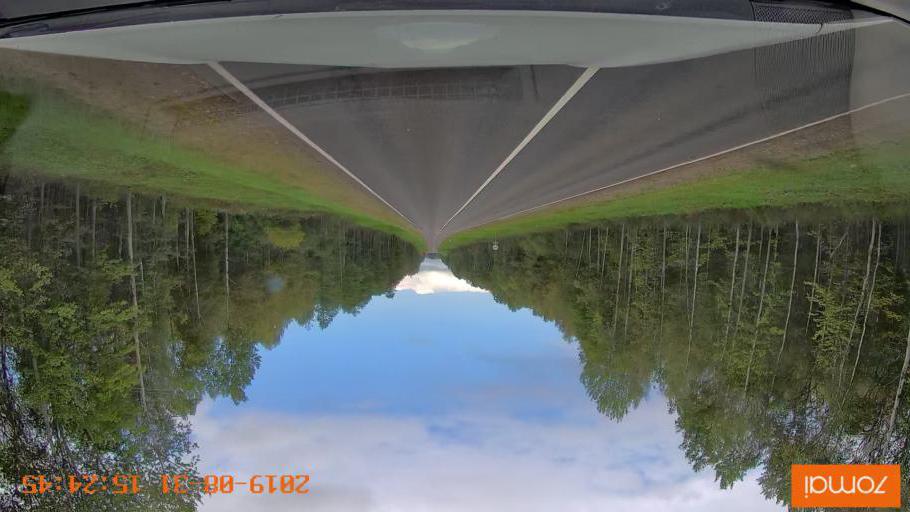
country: RU
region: Kaluga
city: Baryatino
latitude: 54.5320
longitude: 34.5094
